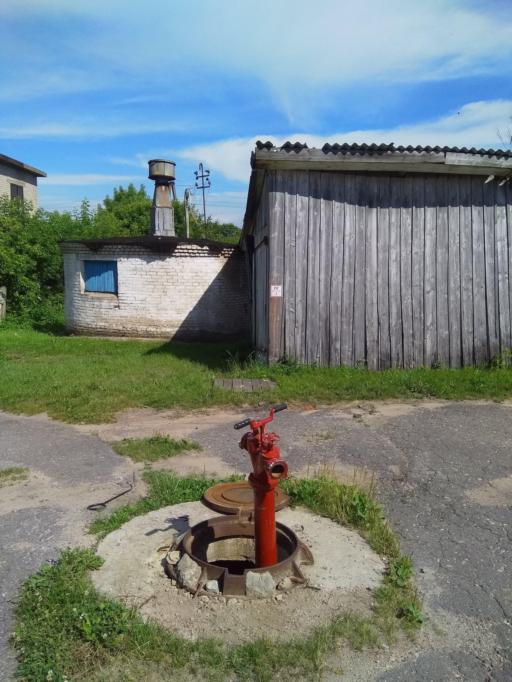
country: BY
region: Mogilev
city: Dashkawka
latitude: 53.7360
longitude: 30.2633
